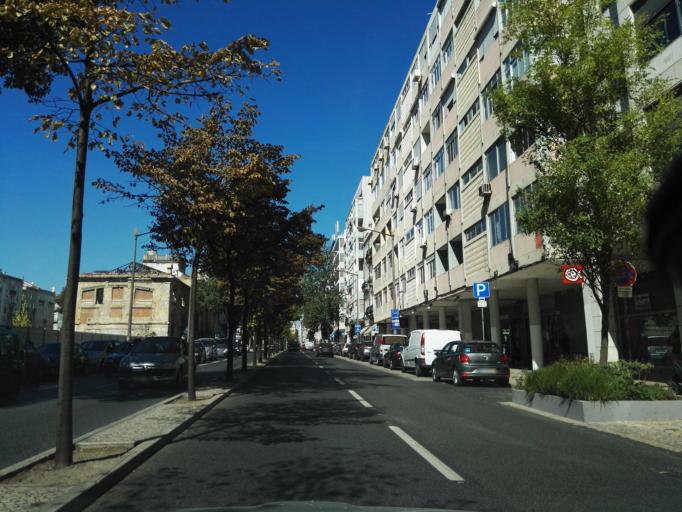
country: PT
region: Lisbon
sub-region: Lisbon
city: Lisbon
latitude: 38.7297
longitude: -9.1346
